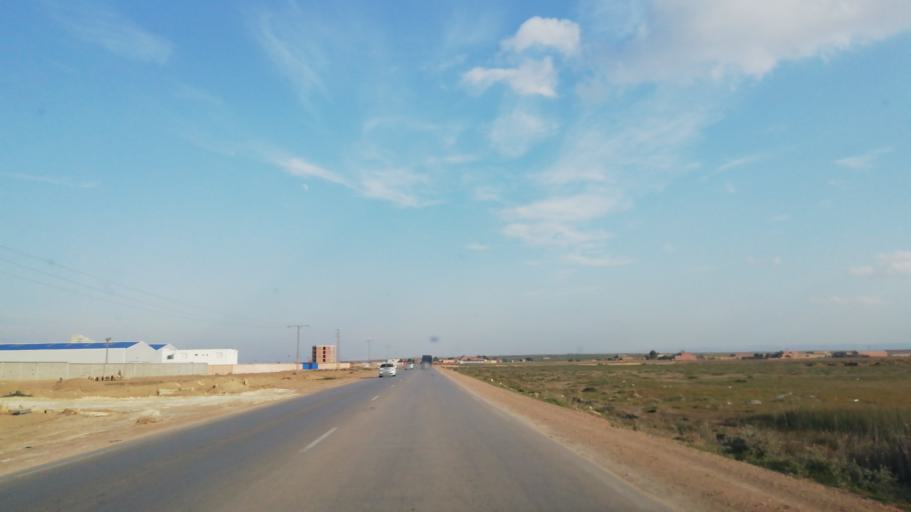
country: DZ
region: Relizane
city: Relizane
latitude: 35.8979
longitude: 0.5771
